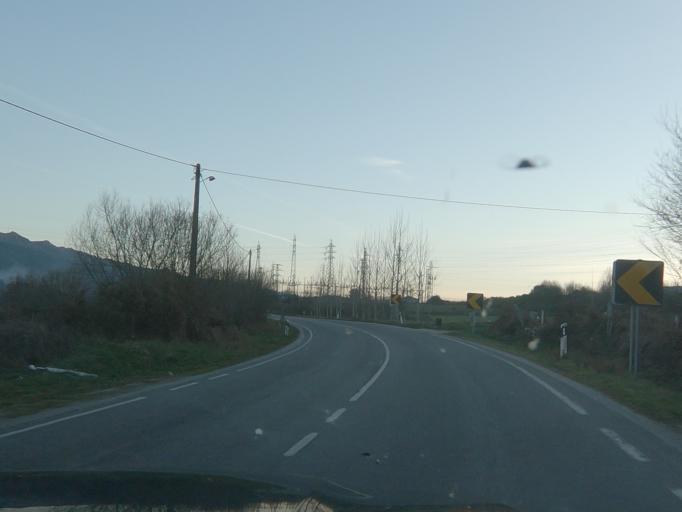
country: PT
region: Vila Real
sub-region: Vila Pouca de Aguiar
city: Vila Pouca de Aguiar
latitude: 41.4670
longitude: -7.6652
